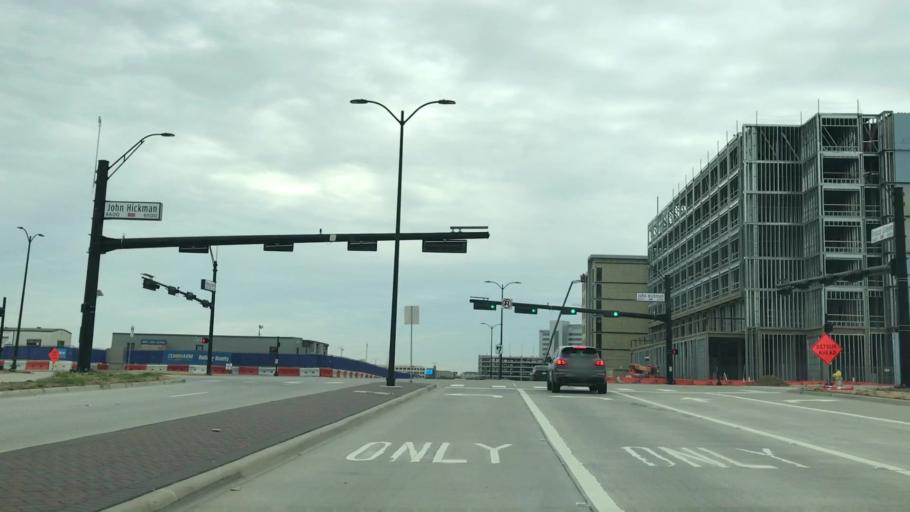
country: US
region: Texas
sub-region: Collin County
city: Frisco
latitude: 33.1161
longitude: -96.8296
